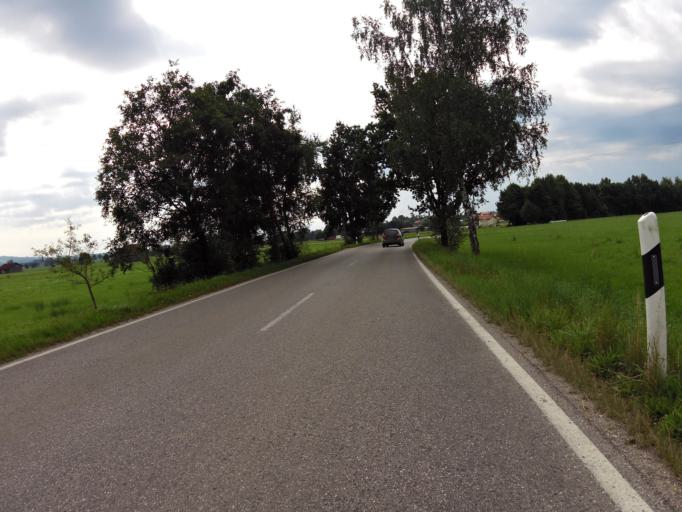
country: DE
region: Bavaria
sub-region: Upper Bavaria
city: Raisting
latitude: 47.9219
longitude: 11.1105
